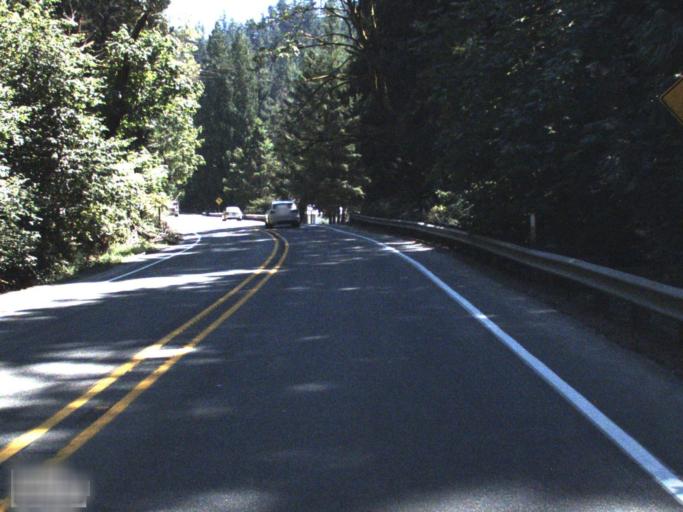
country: US
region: Washington
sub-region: King County
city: Snoqualmie
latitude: 47.5546
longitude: -121.8421
